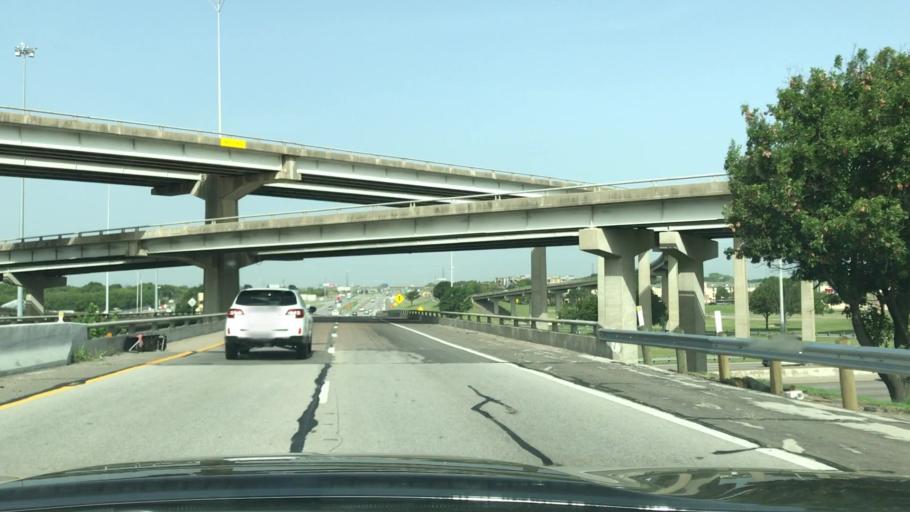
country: US
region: Texas
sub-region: Dallas County
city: Mesquite
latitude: 32.7927
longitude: -96.6244
